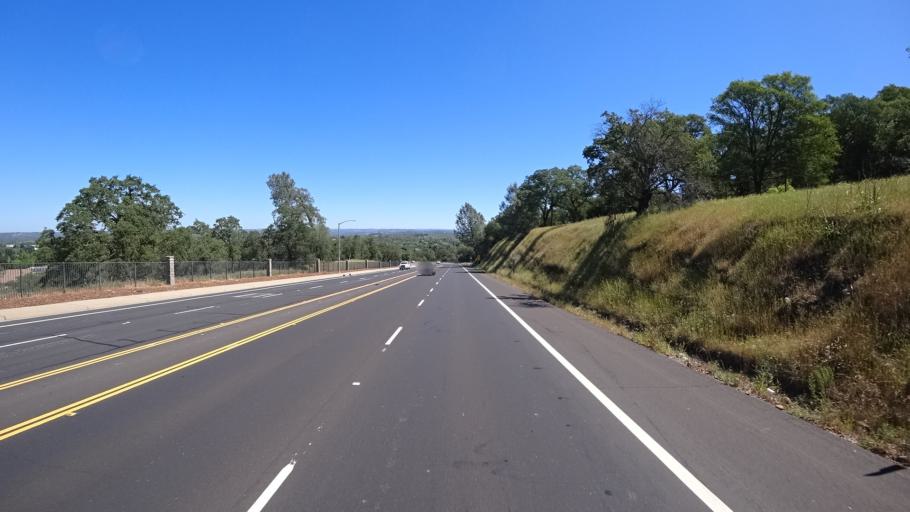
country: US
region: California
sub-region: Placer County
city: Rocklin
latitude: 38.7750
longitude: -121.2052
